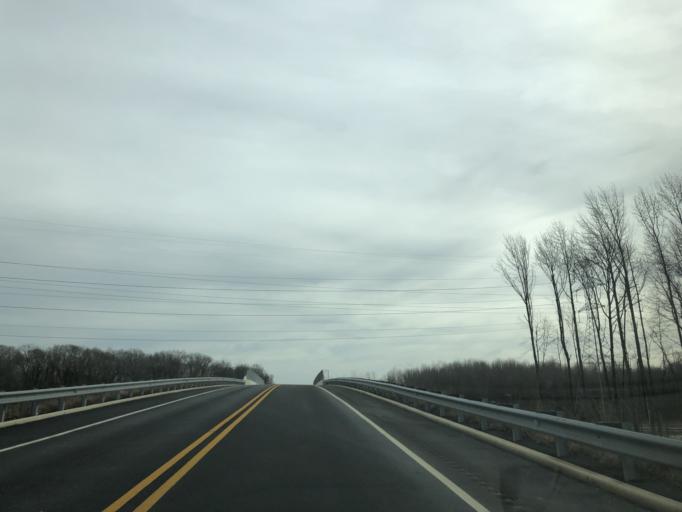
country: US
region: Delaware
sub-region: New Castle County
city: Middletown
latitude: 39.4155
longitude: -75.7681
